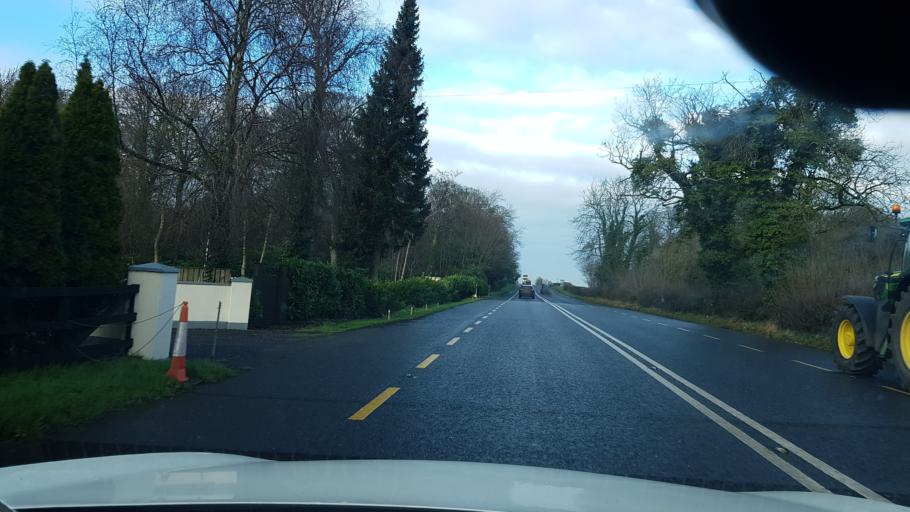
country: IE
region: Leinster
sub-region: An Mhi
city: Navan
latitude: 53.6069
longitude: -6.6248
